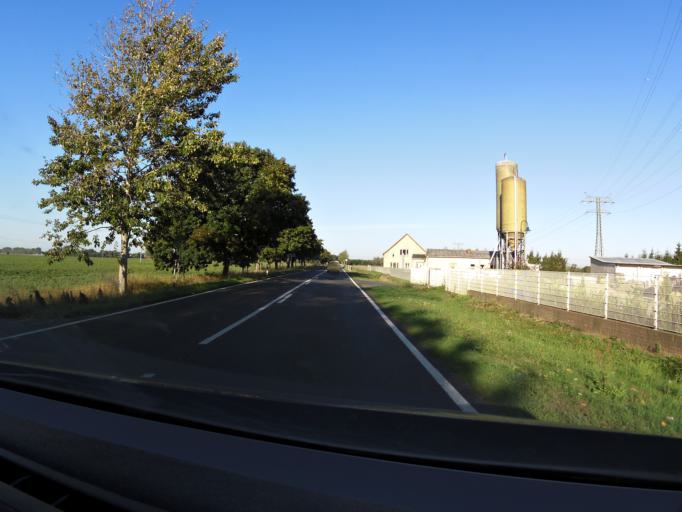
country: DE
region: Mecklenburg-Vorpommern
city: Anklam
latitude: 53.8529
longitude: 13.6562
